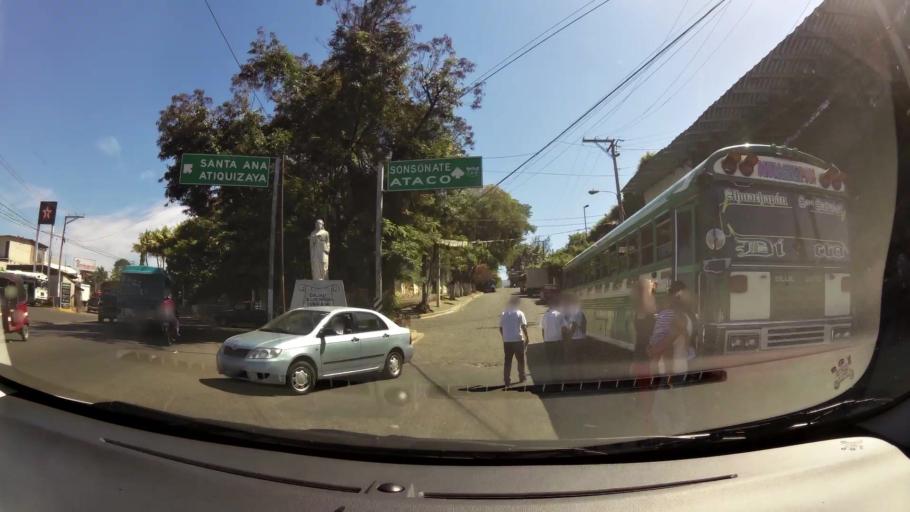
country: SV
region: Ahuachapan
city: Ahuachapan
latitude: 13.9231
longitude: -89.8445
